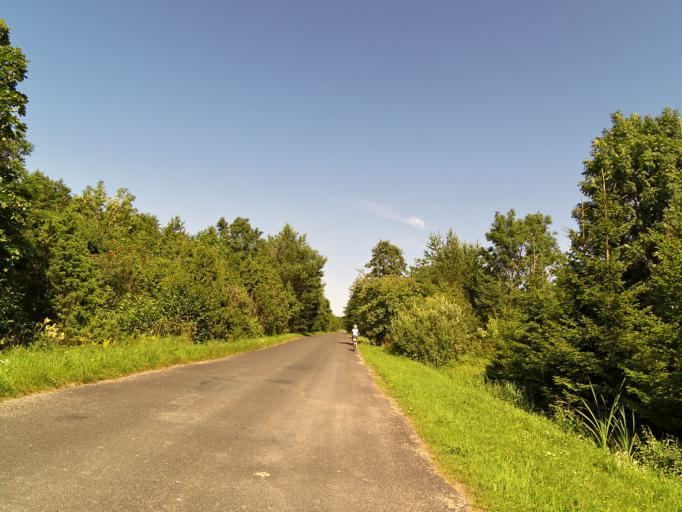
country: EE
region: Hiiumaa
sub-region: Kaerdla linn
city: Kardla
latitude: 58.7815
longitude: 22.4887
